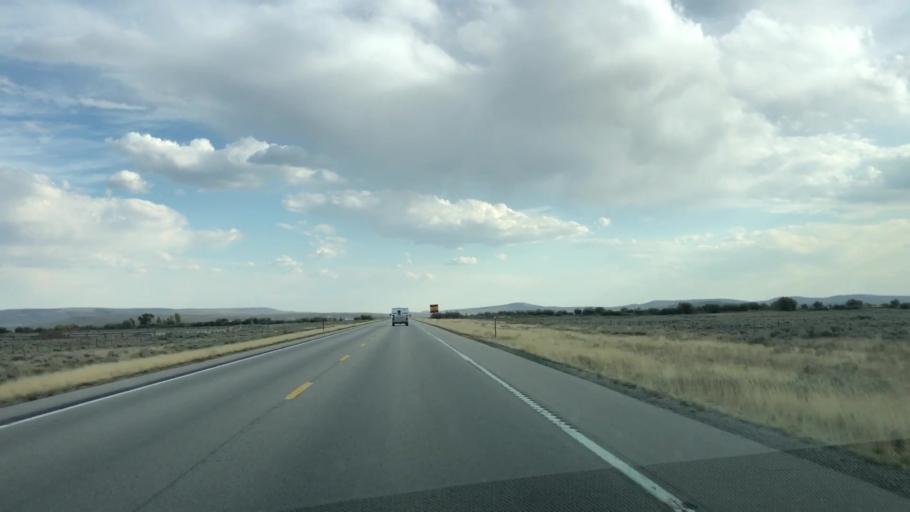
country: US
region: Wyoming
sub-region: Sublette County
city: Pinedale
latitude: 42.9822
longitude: -110.0918
